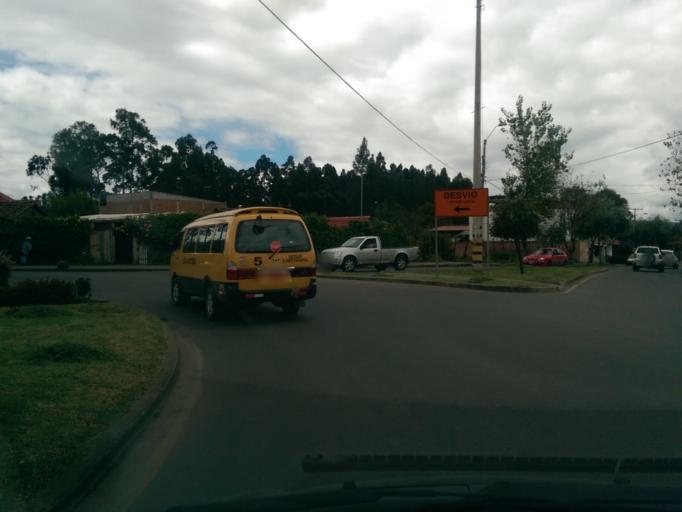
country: EC
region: Azuay
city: Cuenca
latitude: -2.9106
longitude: -79.0197
